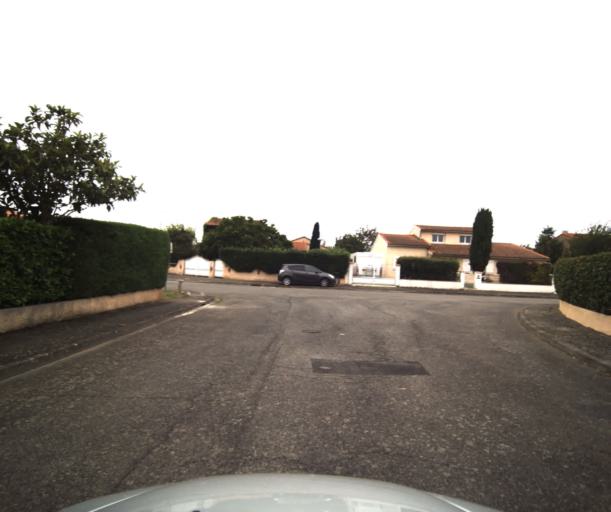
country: FR
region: Midi-Pyrenees
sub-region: Departement de la Haute-Garonne
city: Muret
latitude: 43.4463
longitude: 1.3159
